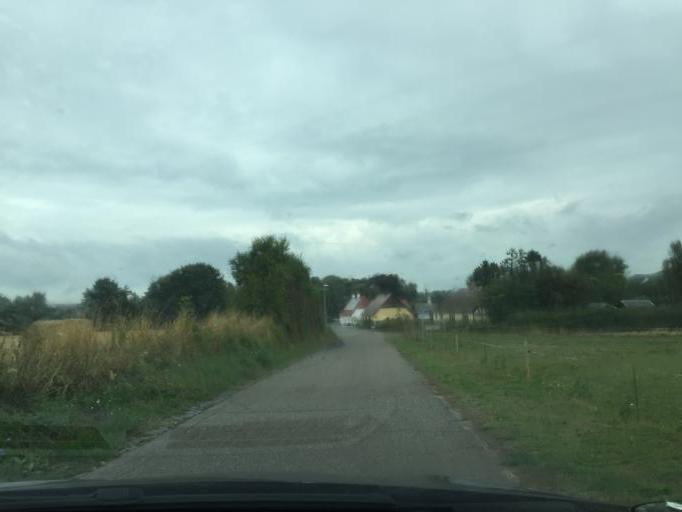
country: DK
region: South Denmark
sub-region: Assens Kommune
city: Assens
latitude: 55.2078
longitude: 10.0019
